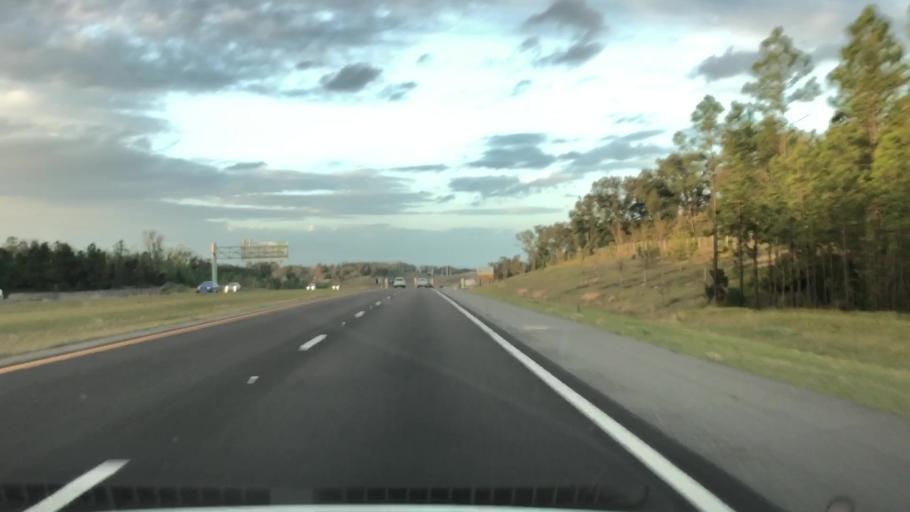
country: US
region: Florida
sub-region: Orange County
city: Zellwood
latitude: 28.7156
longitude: -81.5616
